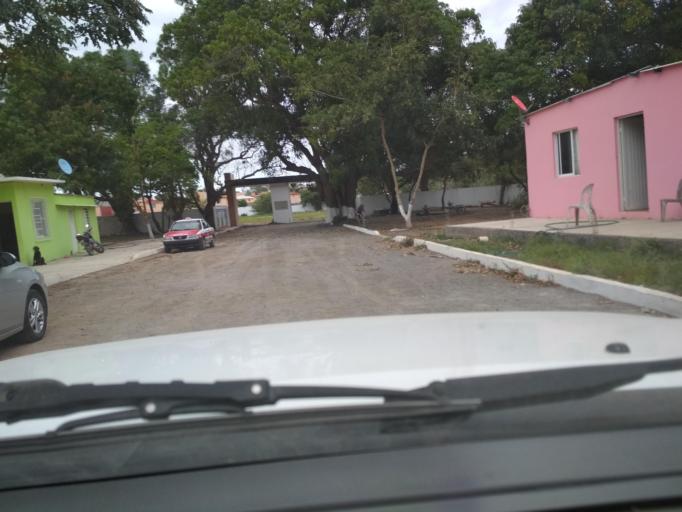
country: MX
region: Veracruz
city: El Tejar
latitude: 19.0739
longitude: -96.1403
